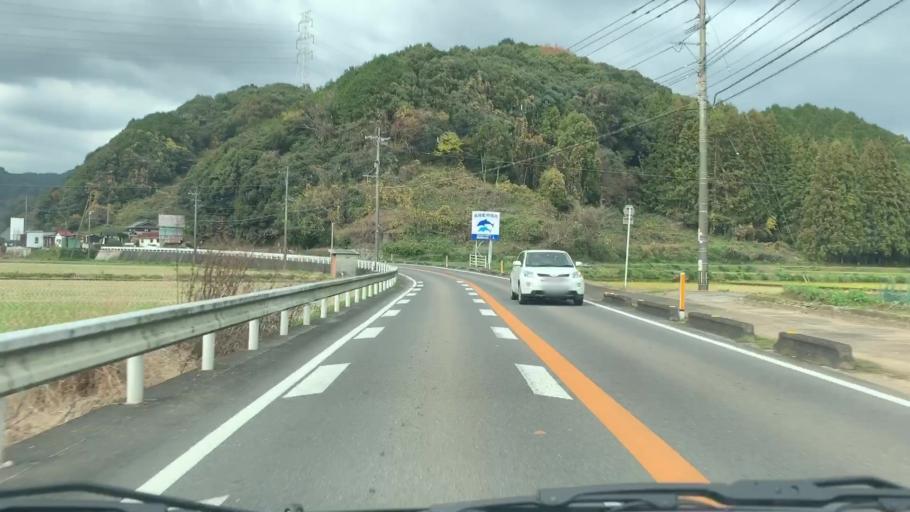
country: JP
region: Saga Prefecture
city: Ureshinomachi-shimojuku
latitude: 33.1341
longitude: 130.0296
